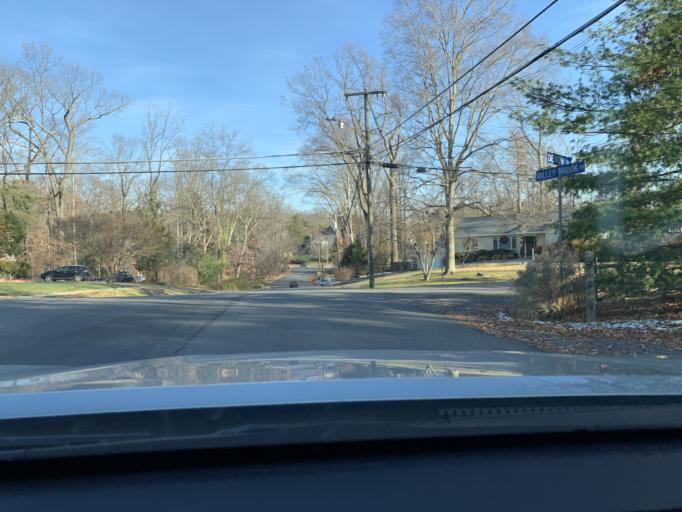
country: US
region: Virginia
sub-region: Fairfax County
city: Jefferson
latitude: 38.8492
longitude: -77.1765
